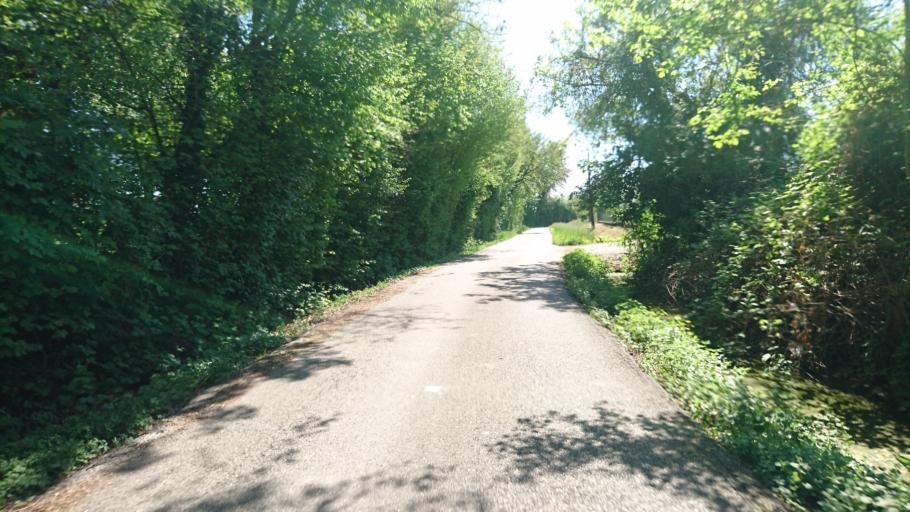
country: IT
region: Veneto
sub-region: Provincia di Treviso
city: Conscio
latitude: 45.6176
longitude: 12.2752
